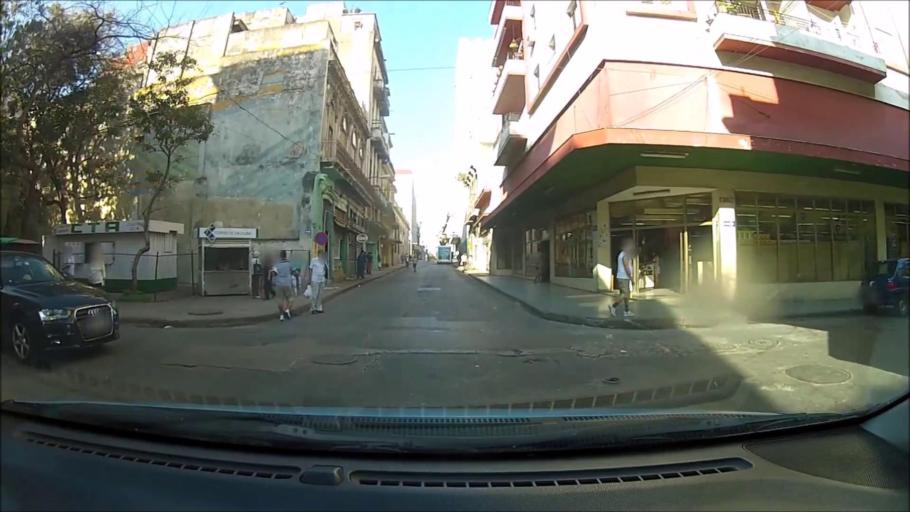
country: CU
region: La Habana
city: Centro Habana
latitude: 23.1376
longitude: -82.3626
